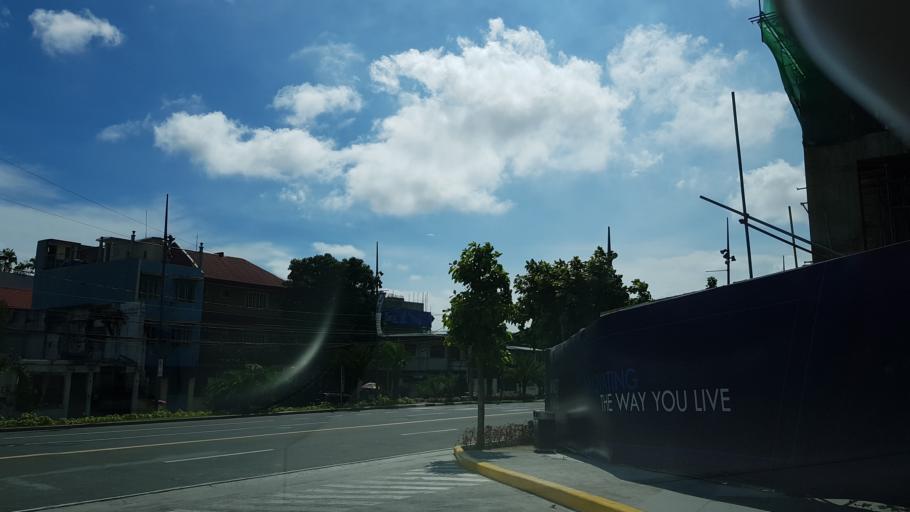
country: PH
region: Metro Manila
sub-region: Mandaluyong
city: Mandaluyong City
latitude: 14.5723
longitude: 121.0190
